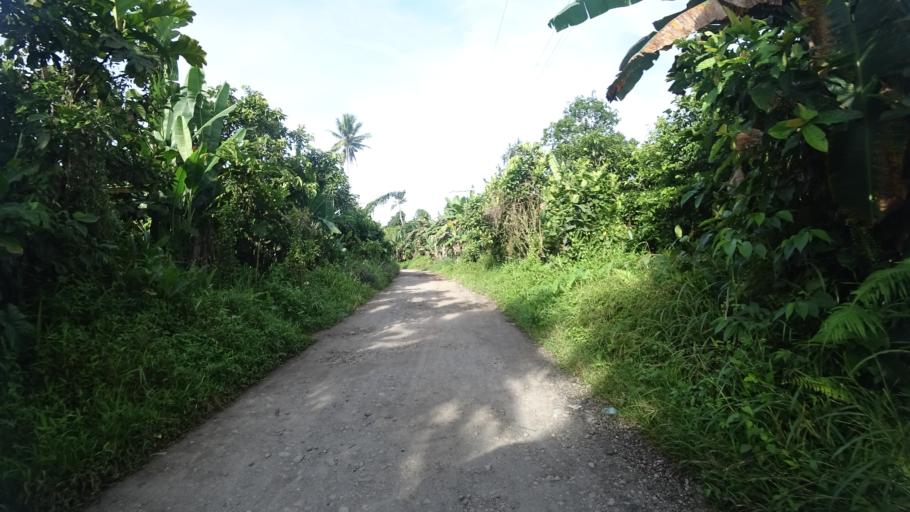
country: PH
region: Eastern Visayas
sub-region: Province of Leyte
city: Pastrana
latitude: 11.1690
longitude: 124.8699
